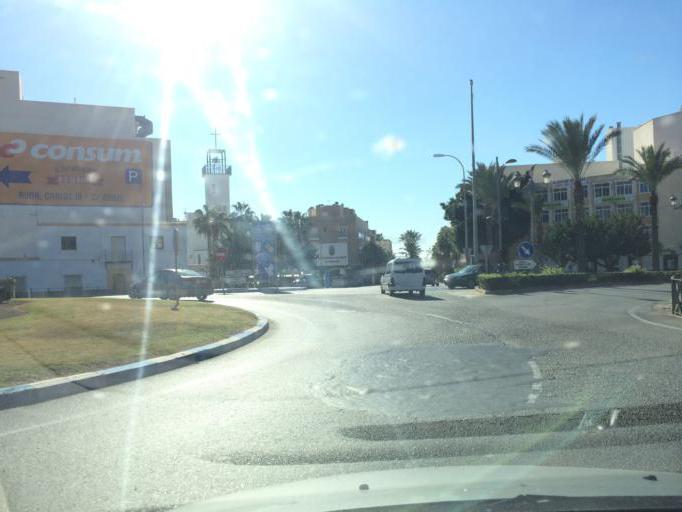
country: ES
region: Andalusia
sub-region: Provincia de Almeria
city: Aguadulce
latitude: 36.8092
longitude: -2.5975
